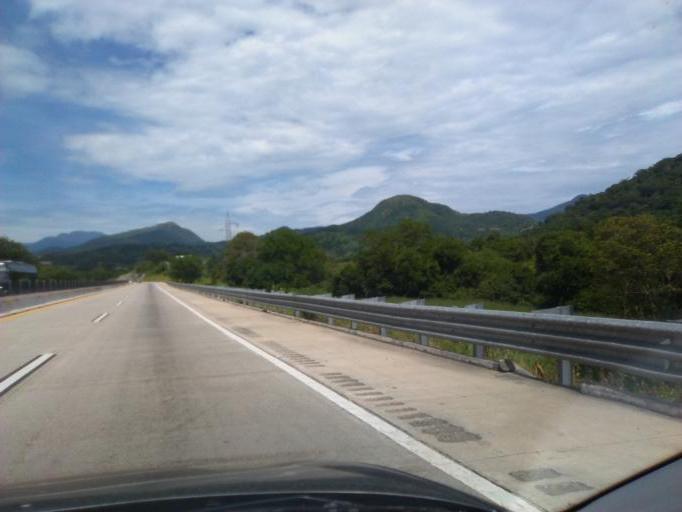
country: MX
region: Guerrero
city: Tierra Colorada
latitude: 17.1557
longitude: -99.5534
